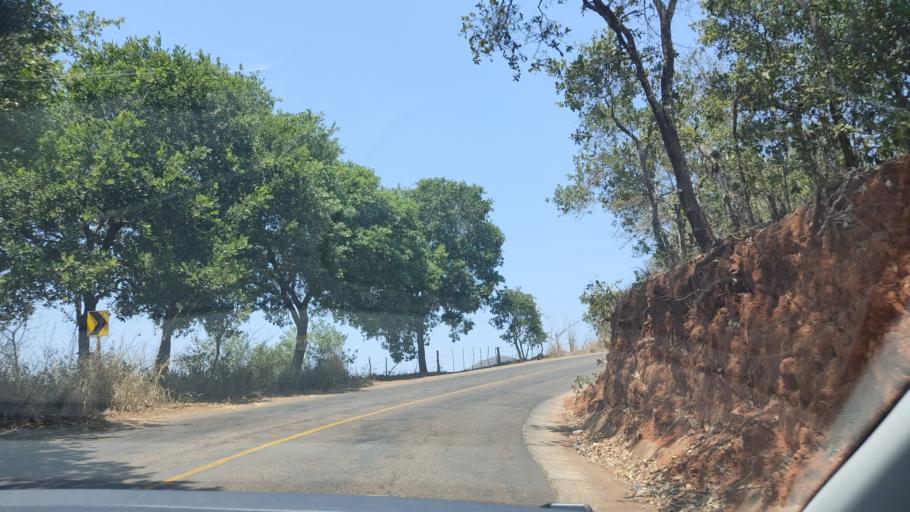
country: MX
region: Nayarit
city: Puga
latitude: 21.5815
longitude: -104.7801
